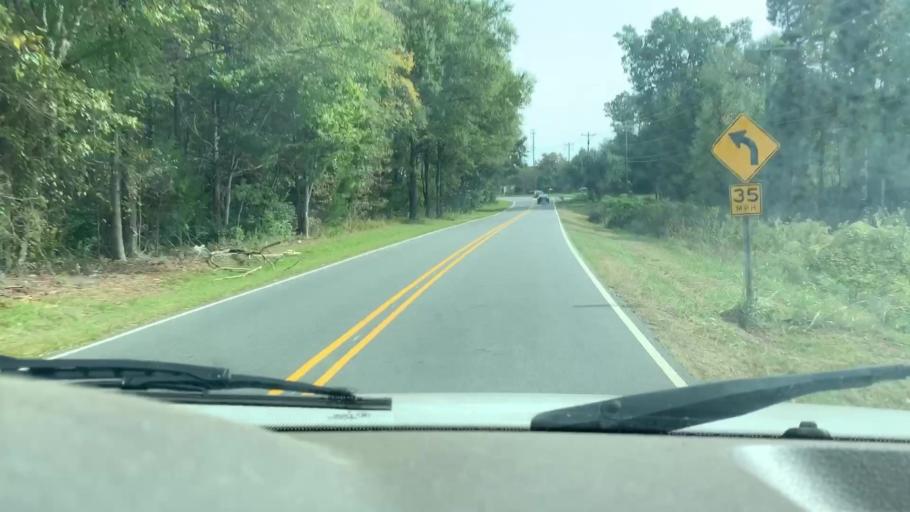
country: US
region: North Carolina
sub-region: Mecklenburg County
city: Huntersville
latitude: 35.4241
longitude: -80.7596
